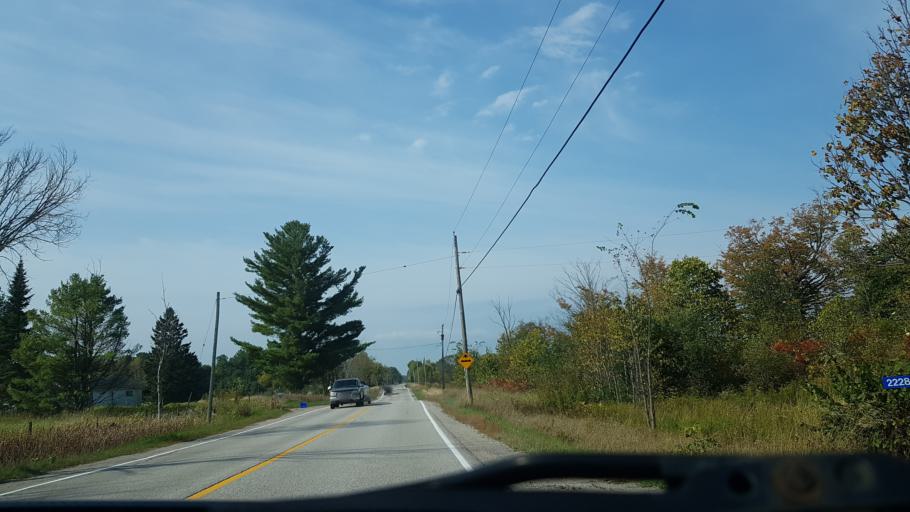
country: CA
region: Ontario
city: Gravenhurst
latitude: 44.7792
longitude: -79.2772
